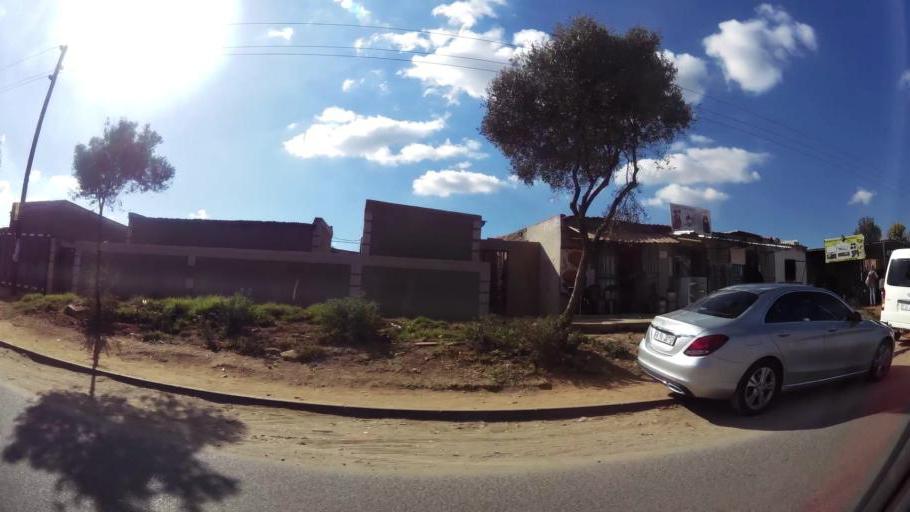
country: ZA
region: Gauteng
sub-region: West Rand District Municipality
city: Muldersdriseloop
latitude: -26.0319
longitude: 27.9256
